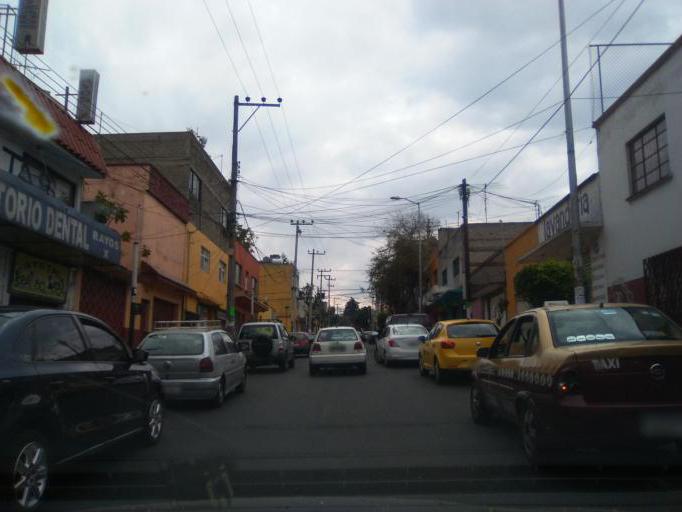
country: MX
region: Mexico City
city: Alvaro Obregon
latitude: 19.3709
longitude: -99.2210
